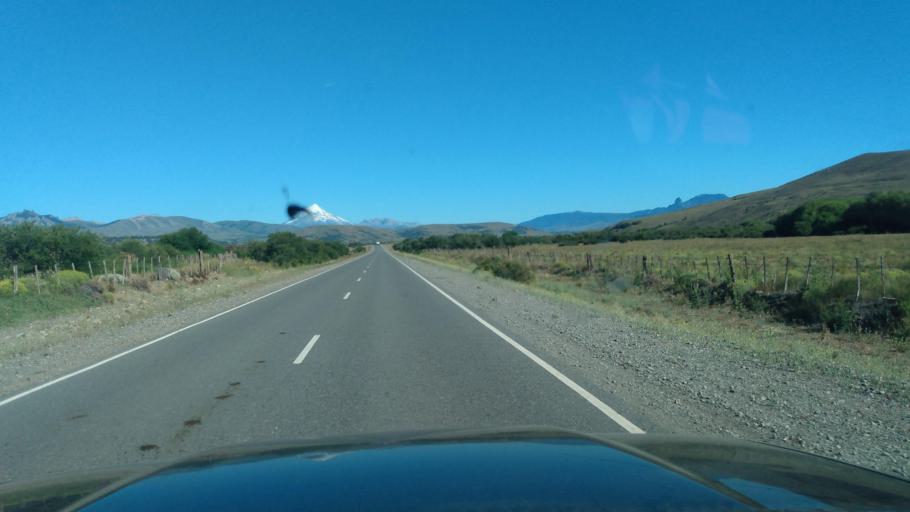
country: AR
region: Neuquen
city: Junin de los Andes
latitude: -39.8880
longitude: -71.1551
